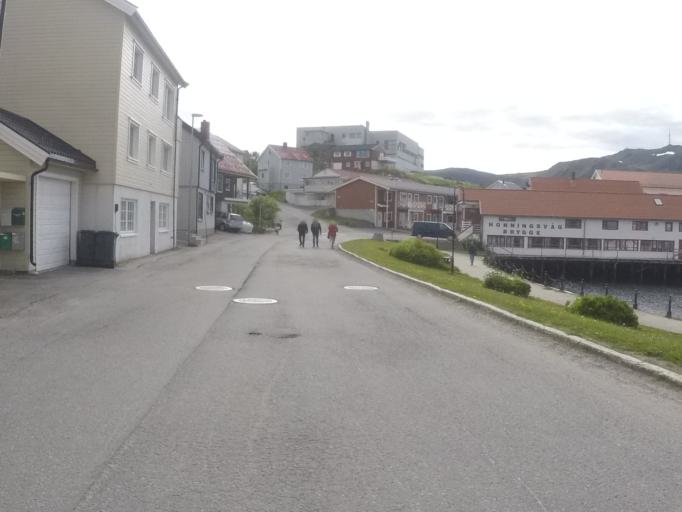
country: NO
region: Finnmark Fylke
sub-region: Nordkapp
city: Honningsvag
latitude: 70.9792
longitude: 25.9756
